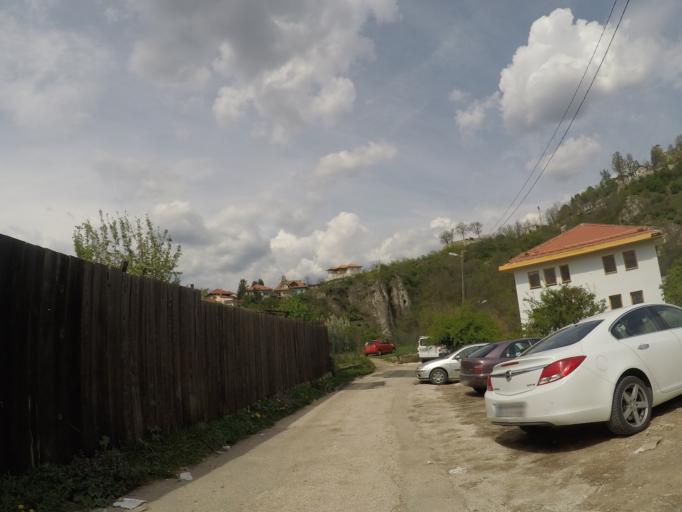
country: BA
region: Federation of Bosnia and Herzegovina
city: Kobilja Glava
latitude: 43.8589
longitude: 18.4370
